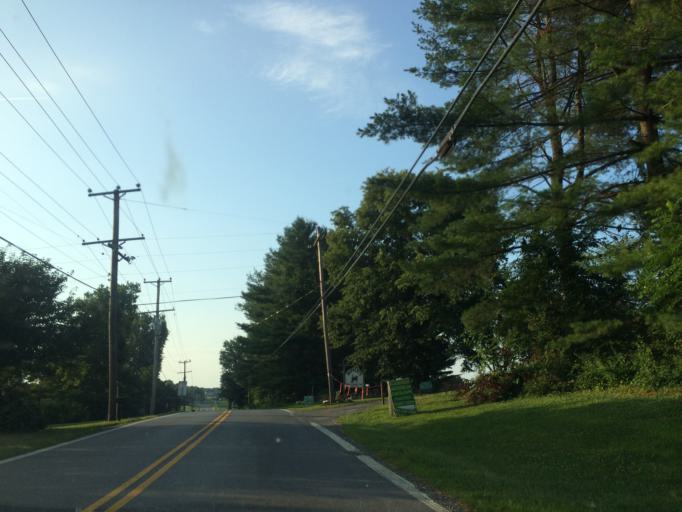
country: US
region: Maryland
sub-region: Carroll County
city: Eldersburg
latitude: 39.3833
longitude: -76.9198
